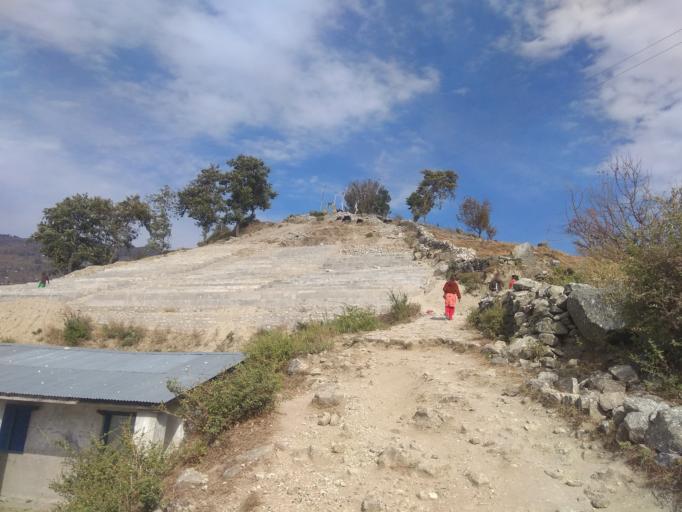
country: NP
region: Far Western
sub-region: Seti Zone
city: Achham
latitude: 29.2371
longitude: 81.6353
